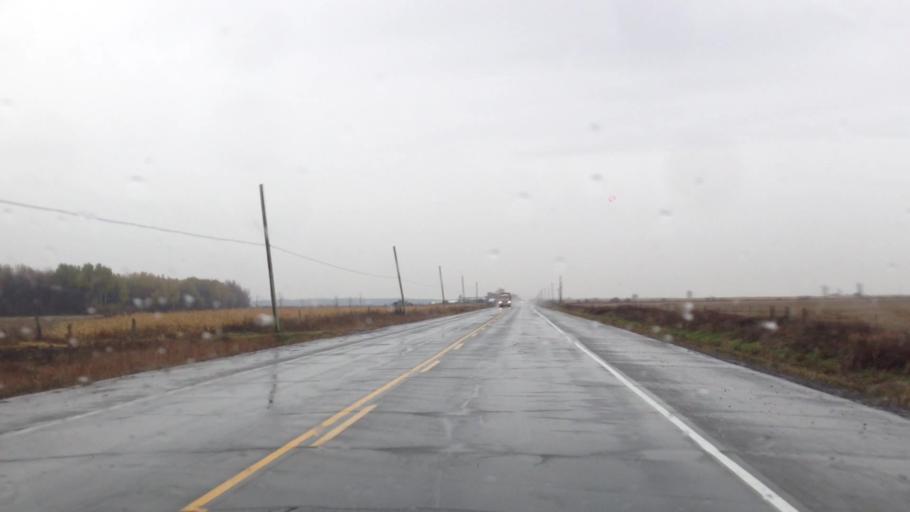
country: CA
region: Ontario
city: Clarence-Rockland
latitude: 45.4698
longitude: -75.4349
